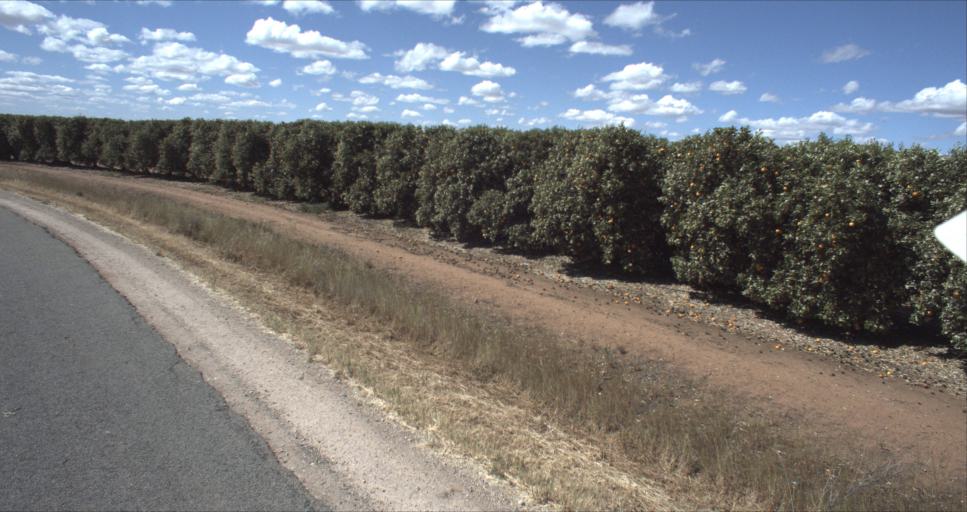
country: AU
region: New South Wales
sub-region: Leeton
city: Leeton
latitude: -34.5087
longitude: 146.2244
